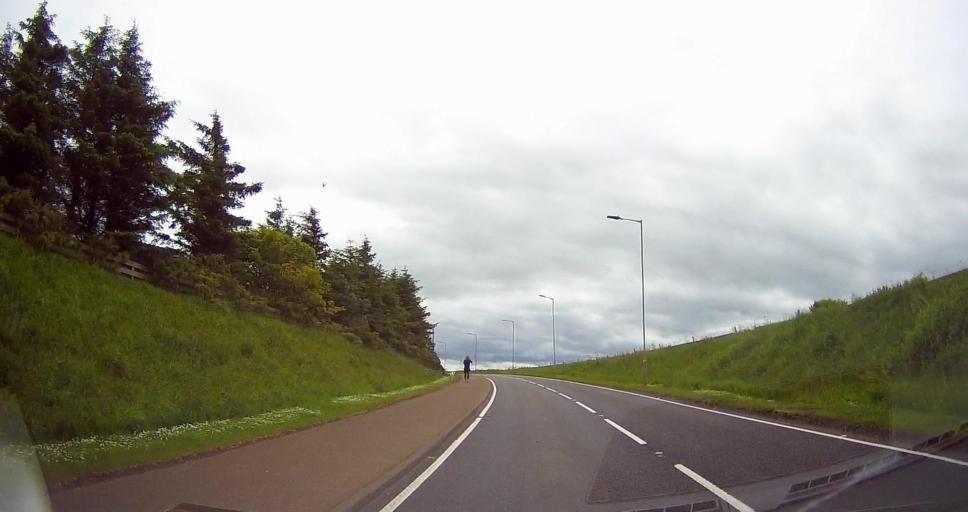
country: GB
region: Scotland
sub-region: Highland
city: Thurso
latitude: 58.6057
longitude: -3.5512
